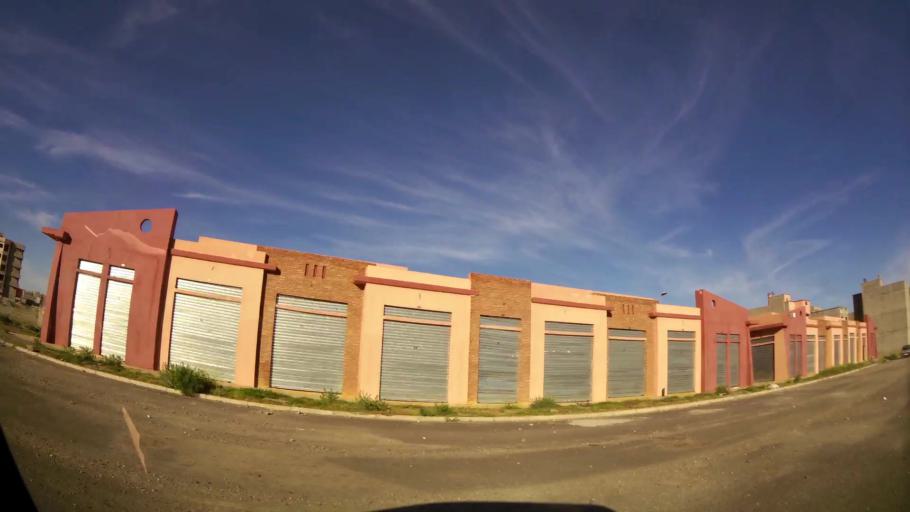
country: MA
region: Marrakech-Tensift-Al Haouz
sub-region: Marrakech
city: Marrakesh
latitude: 31.7626
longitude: -8.1043
